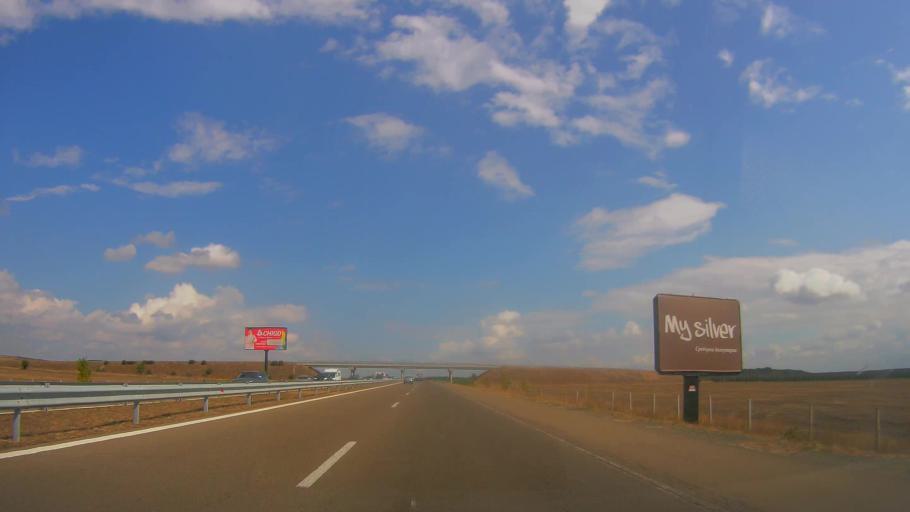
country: BG
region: Burgas
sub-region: Obshtina Karnobat
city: Karnobat
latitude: 42.5898
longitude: 27.0087
